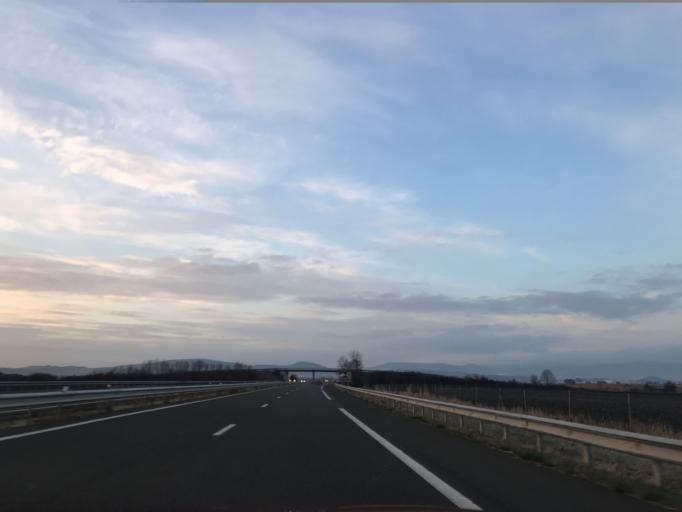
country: FR
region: Auvergne
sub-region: Departement du Puy-de-Dome
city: Pont-du-Chateau
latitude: 45.8068
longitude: 3.2191
